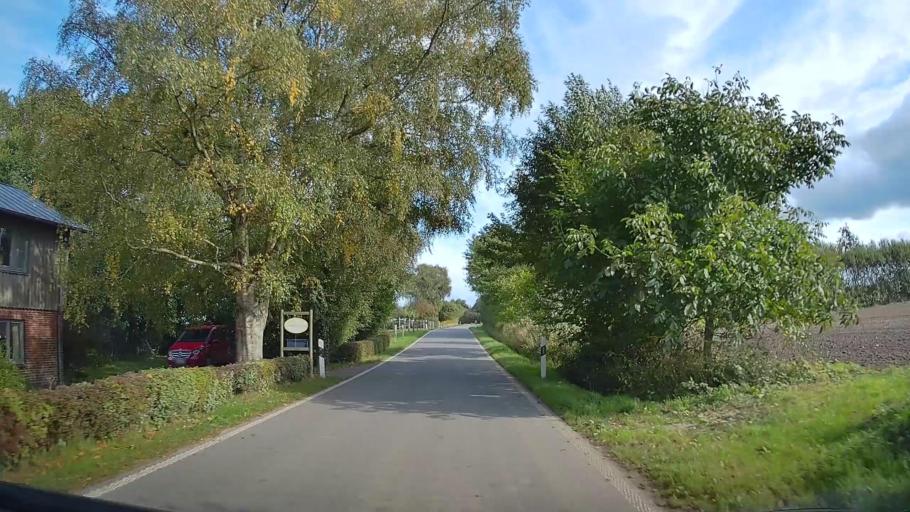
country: DE
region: Schleswig-Holstein
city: Steinbergkirche
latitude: 54.8027
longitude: 9.7380
